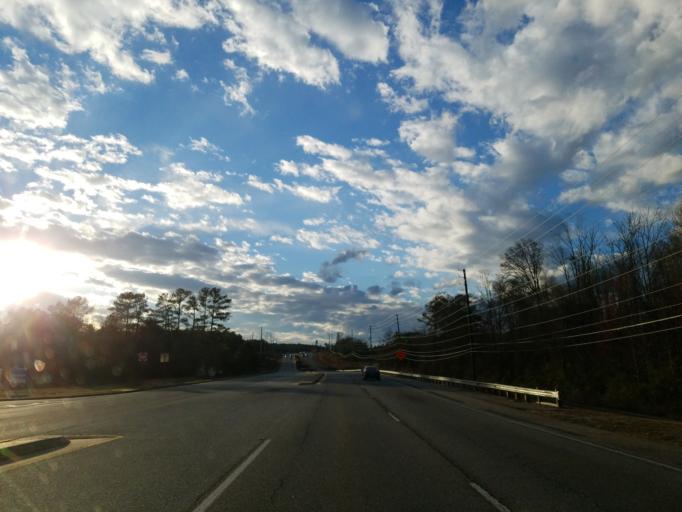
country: US
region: Georgia
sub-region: Henry County
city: McDonough
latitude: 33.4595
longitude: -84.1859
